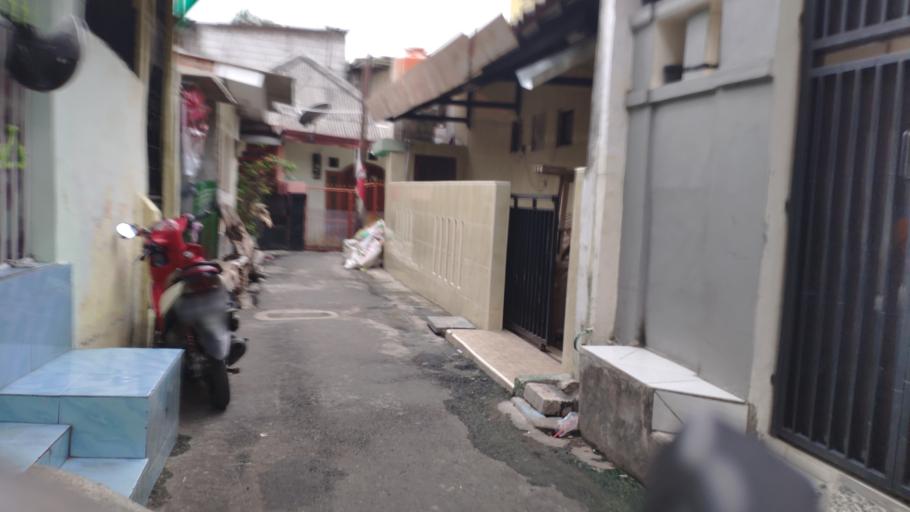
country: ID
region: Jakarta Raya
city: Jakarta
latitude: -6.2112
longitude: 106.8383
